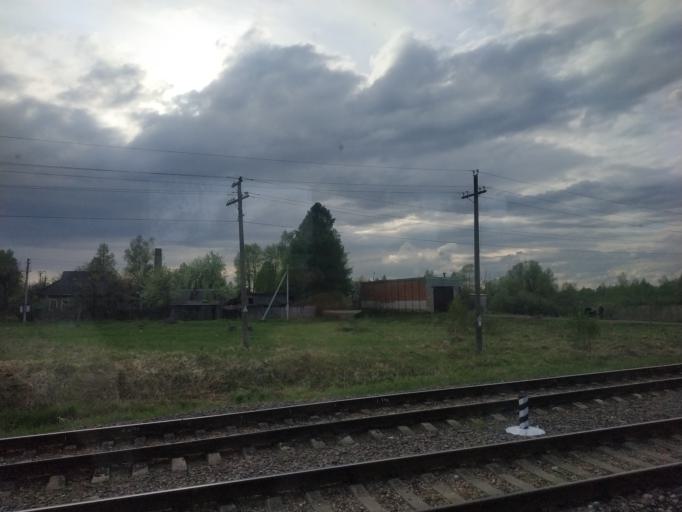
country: RU
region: Smolensk
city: Ugra
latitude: 54.7729
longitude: 34.3428
